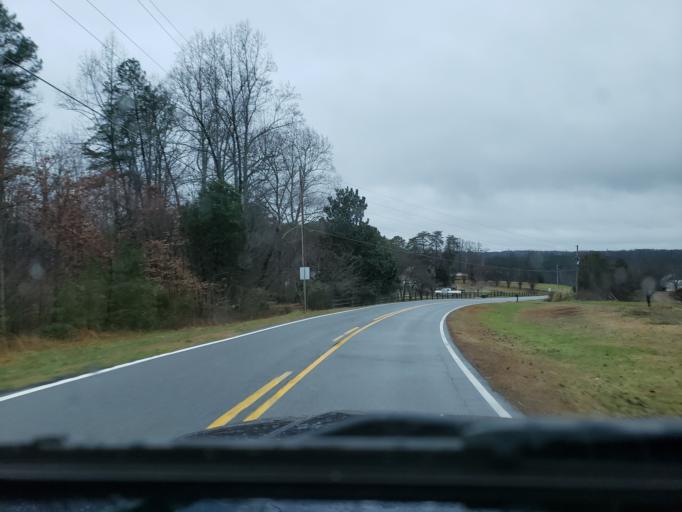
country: US
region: North Carolina
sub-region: Cleveland County
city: White Plains
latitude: 35.1783
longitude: -81.3688
